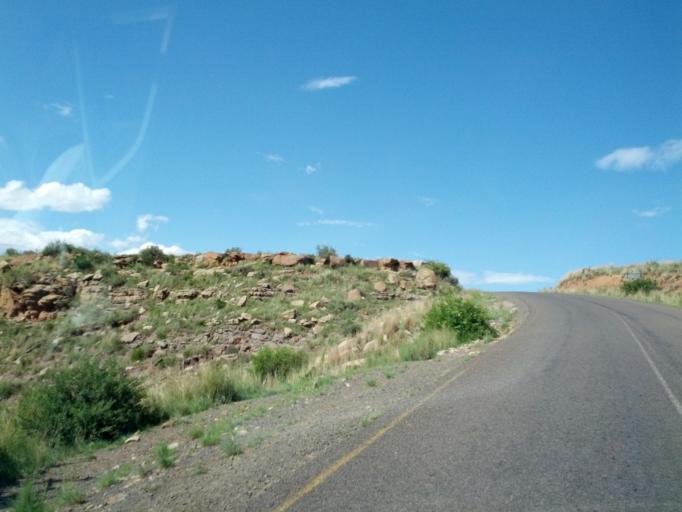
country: LS
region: Qacha's Nek
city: Qacha's Nek
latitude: -30.0540
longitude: 28.4851
